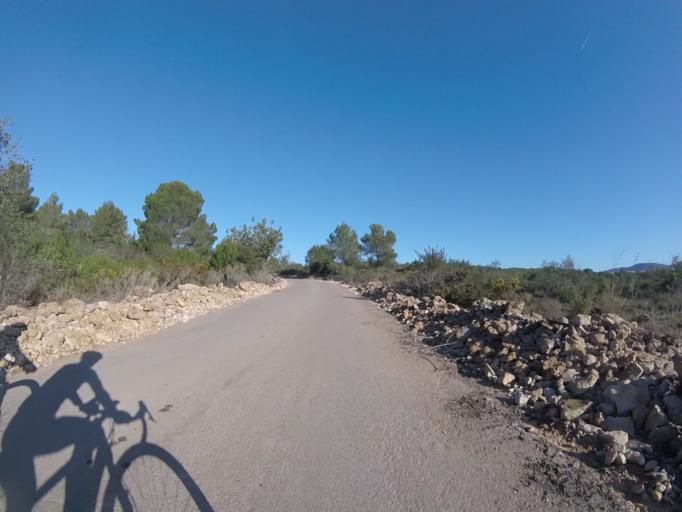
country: ES
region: Valencia
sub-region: Provincia de Castello
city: Alcala de Xivert
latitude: 40.2688
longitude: 0.2075
